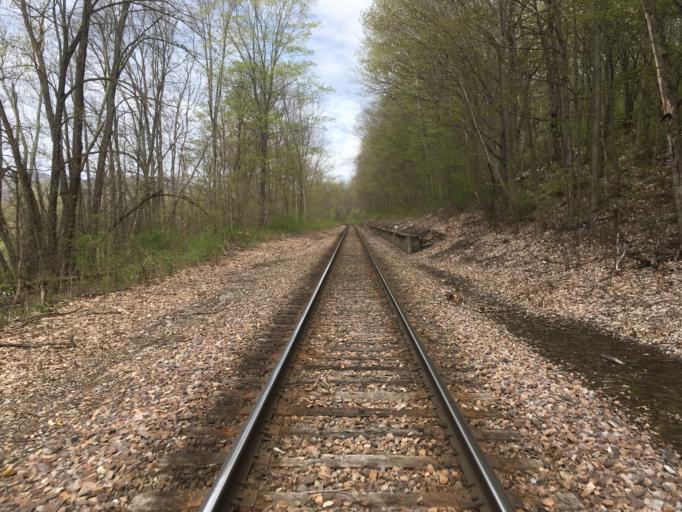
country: US
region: Vermont
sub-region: Rutland County
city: Brandon
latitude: 43.7120
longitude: -73.0394
